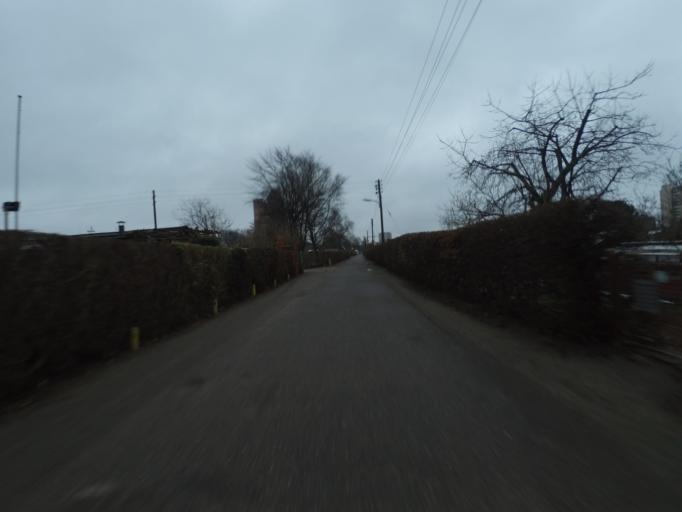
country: DE
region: Hamburg
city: Stellingen
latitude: 53.5874
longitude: 9.9370
